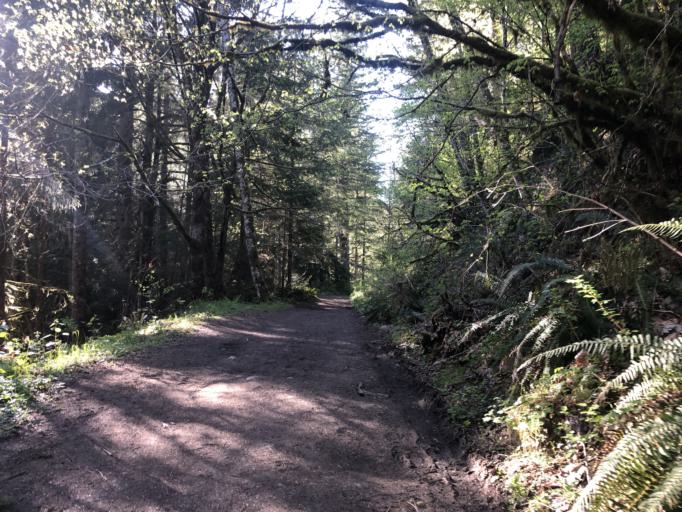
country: US
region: Washington
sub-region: Pierce County
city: Buckley
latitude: 47.0397
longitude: -122.0380
